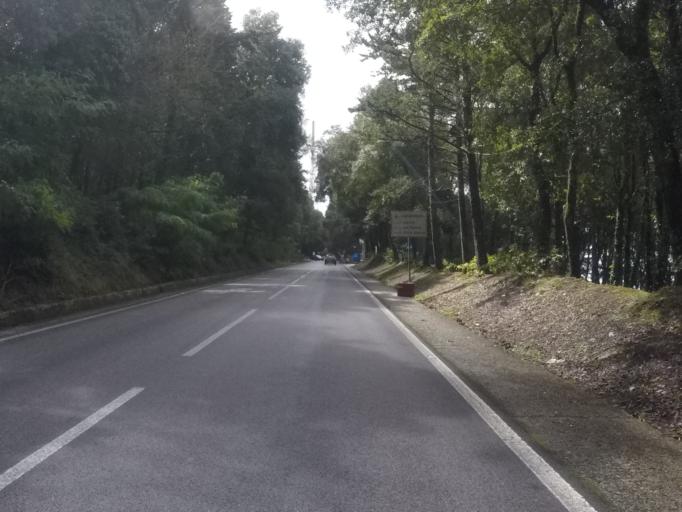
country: IT
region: Sicily
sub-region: Trapani
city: Erice
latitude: 38.0394
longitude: 12.5841
